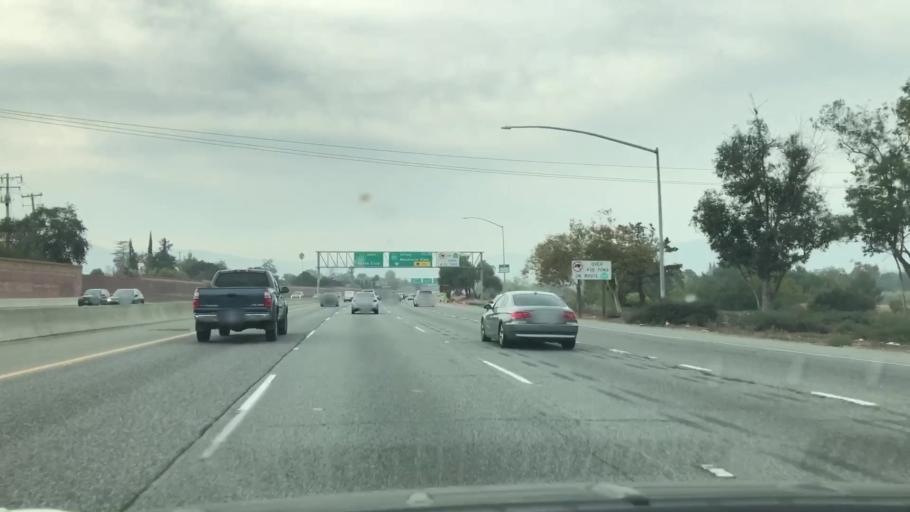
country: US
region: California
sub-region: Santa Clara County
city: Cambrian Park
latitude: 37.2654
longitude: -121.9480
